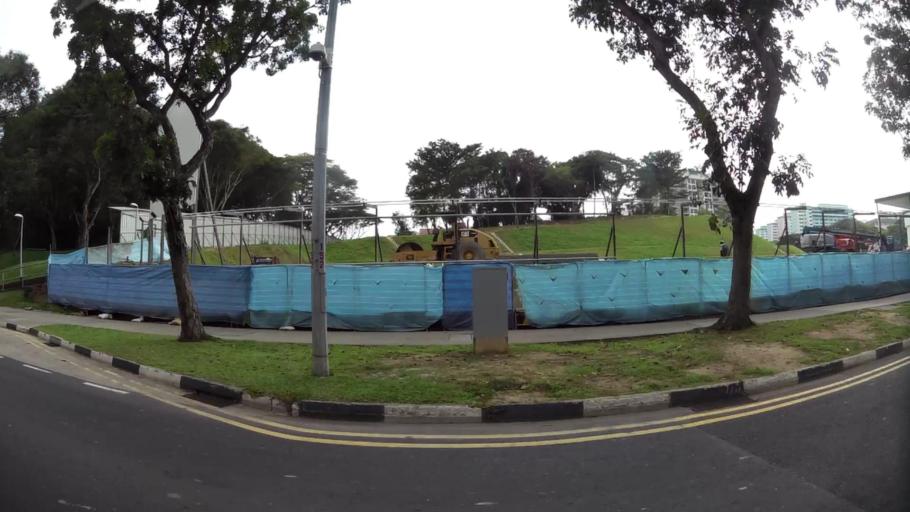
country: SG
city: Singapore
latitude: 1.3266
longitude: 103.9453
